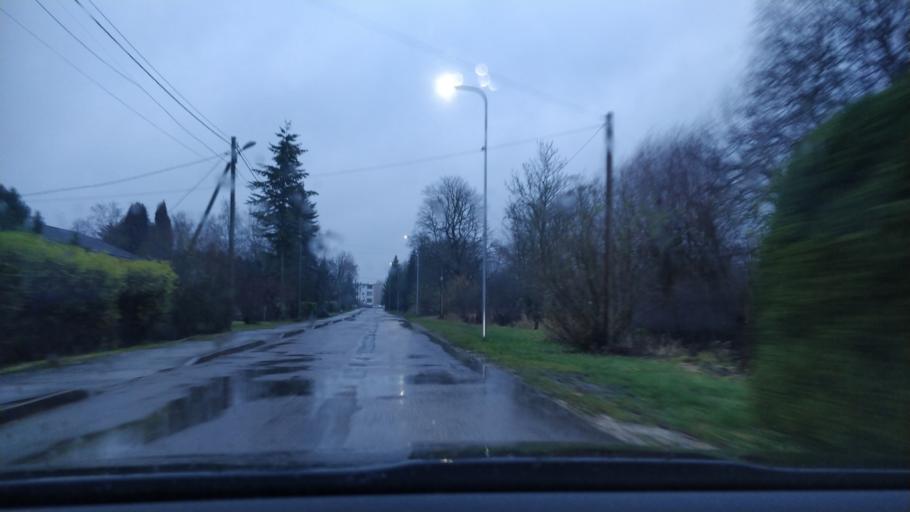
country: EE
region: Laeaene
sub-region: Lihula vald
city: Lihula
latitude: 58.6890
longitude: 23.8380
